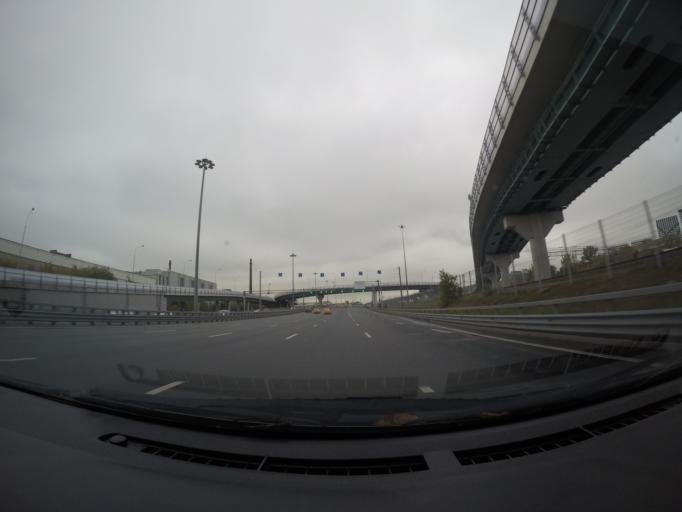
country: RU
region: Moscow
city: Ryazanskiy
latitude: 55.7627
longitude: 37.7473
